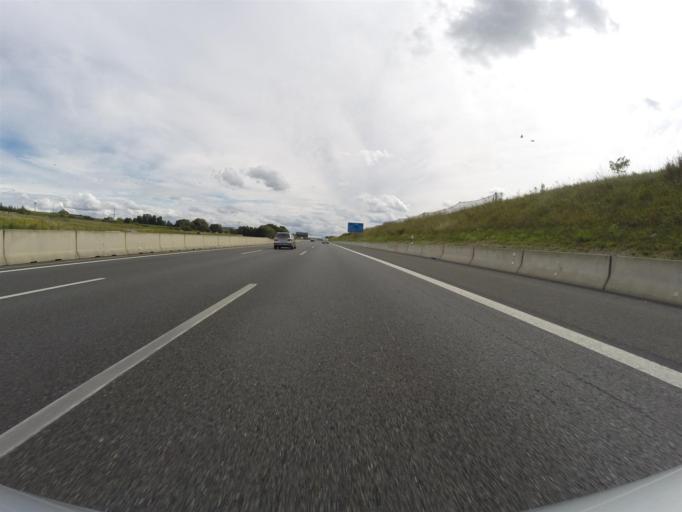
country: DE
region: Bavaria
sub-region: Upper Franconia
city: Bayreuth
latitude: 49.9257
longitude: 11.6025
